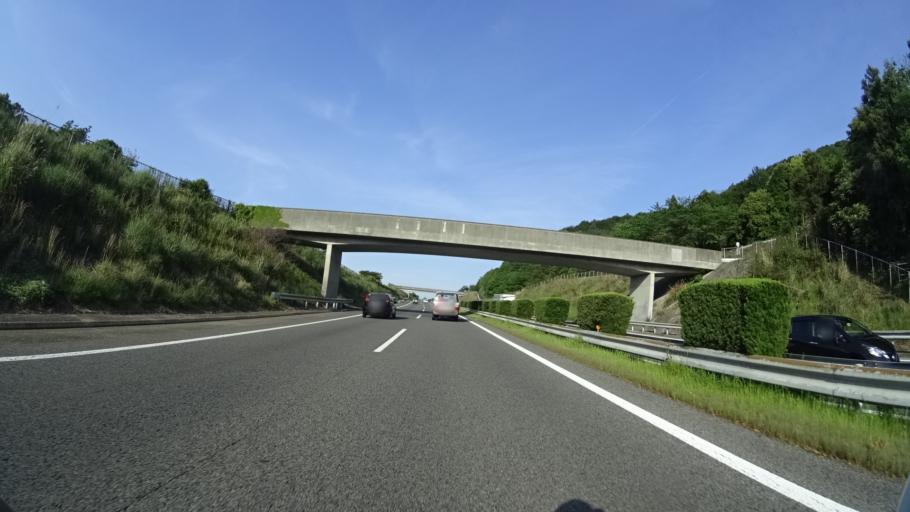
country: JP
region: Ehime
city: Niihama
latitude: 33.9509
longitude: 133.4365
